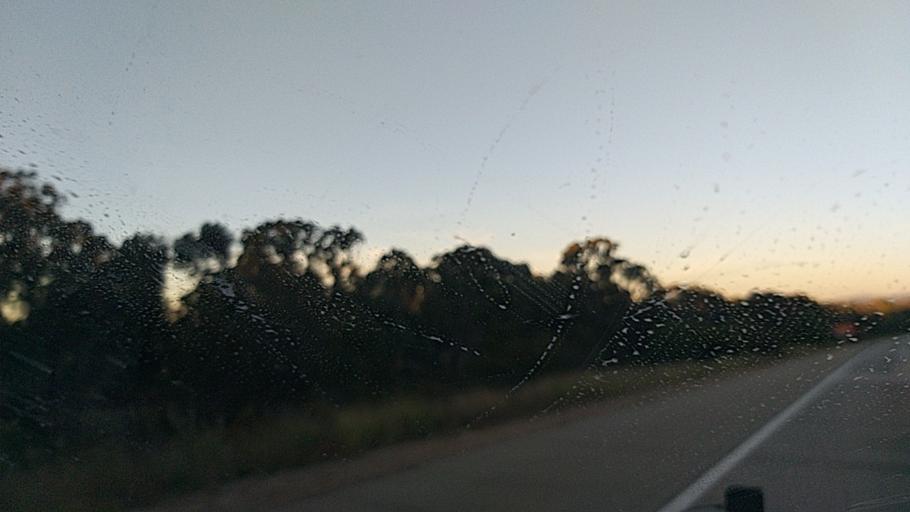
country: AU
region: New South Wales
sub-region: Goulburn Mulwaree
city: Goulburn
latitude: -34.7724
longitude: 149.7560
